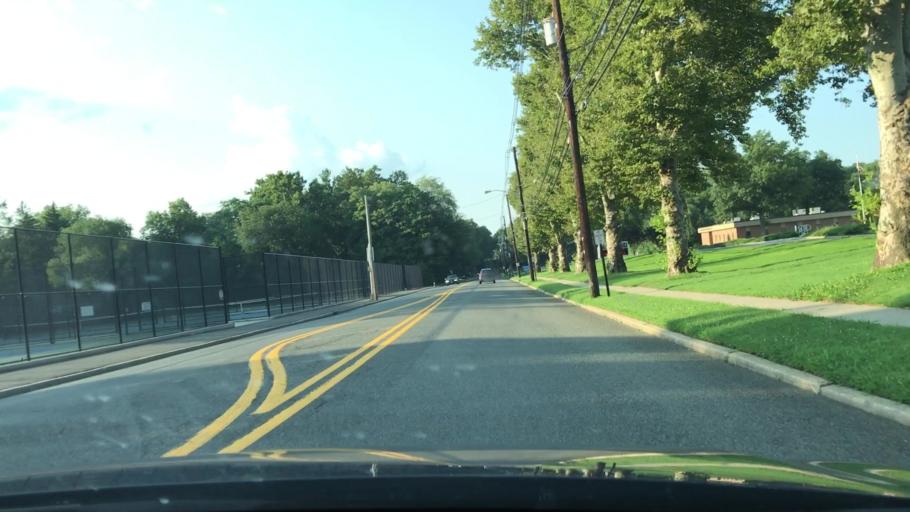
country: US
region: New Jersey
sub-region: Bergen County
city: Demarest
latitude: 40.9626
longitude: -73.9746
